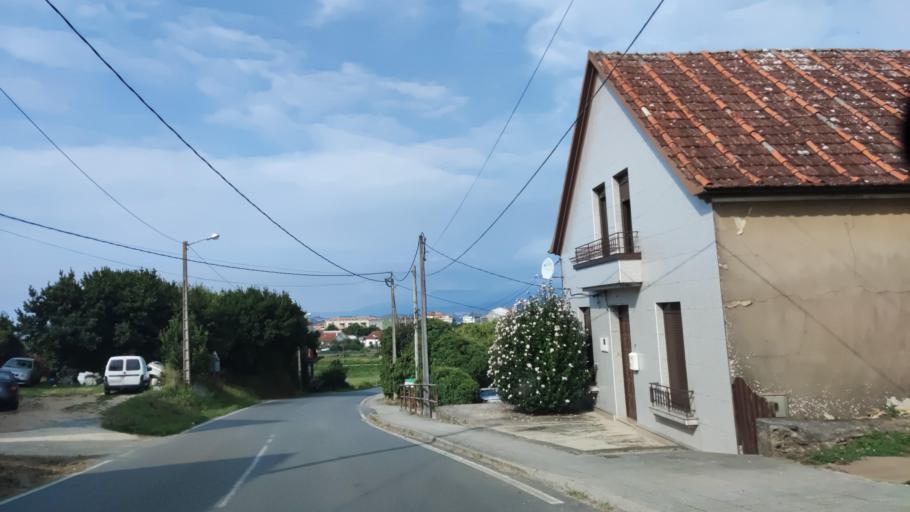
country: ES
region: Galicia
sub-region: Provincia da Coruna
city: Rianxo
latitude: 42.6484
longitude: -8.8113
